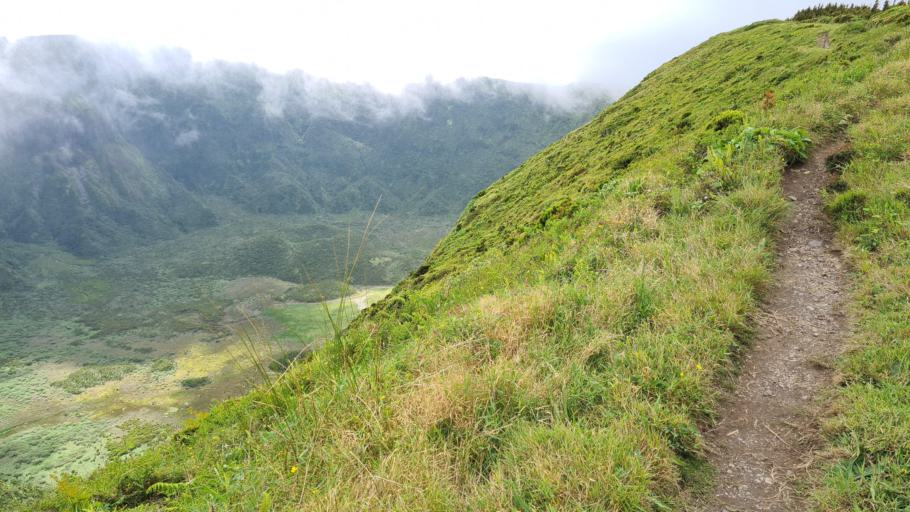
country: PT
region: Azores
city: Ribeira Grande
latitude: 38.5877
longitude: -28.7019
